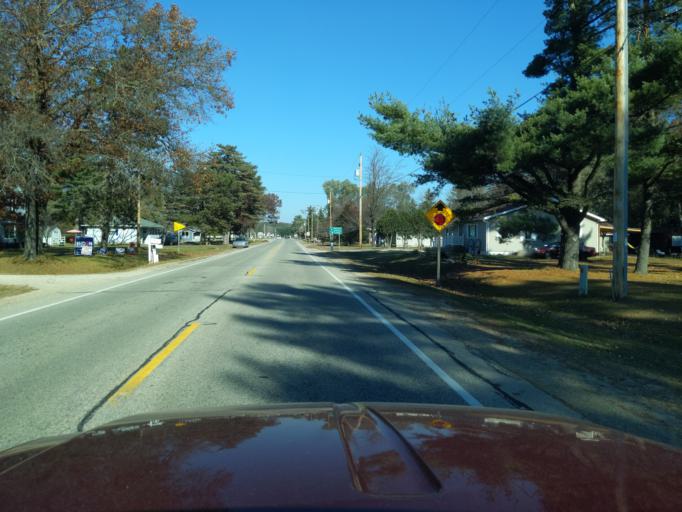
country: US
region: Wisconsin
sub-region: Waushara County
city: Wautoma
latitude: 44.0663
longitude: -89.2975
